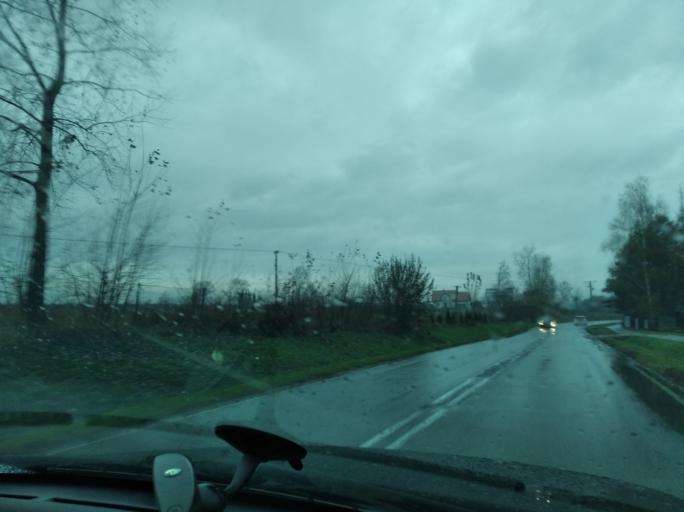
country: PL
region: Subcarpathian Voivodeship
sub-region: Powiat lancucki
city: Albigowa
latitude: 50.0328
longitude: 22.2285
